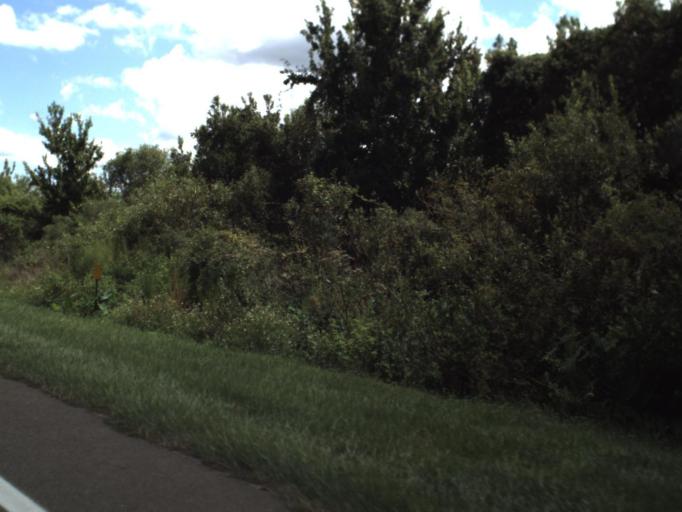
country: US
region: Florida
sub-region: Polk County
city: Lake Alfred
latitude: 28.0695
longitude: -81.6892
